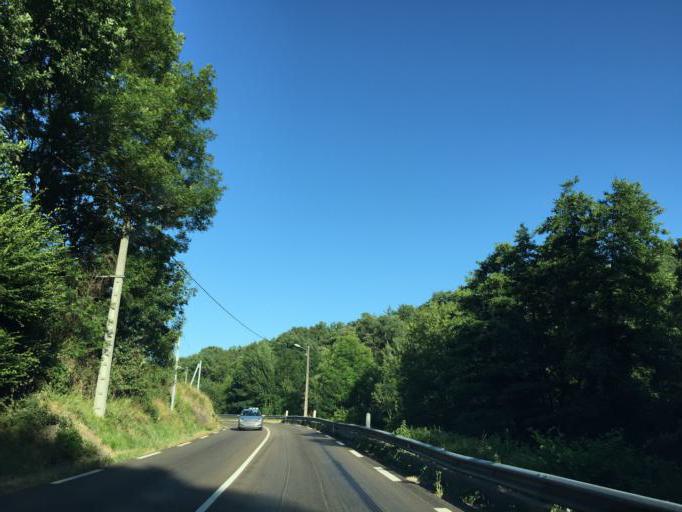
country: FR
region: Rhone-Alpes
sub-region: Departement de la Loire
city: Sorbiers
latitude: 45.4725
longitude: 4.4836
